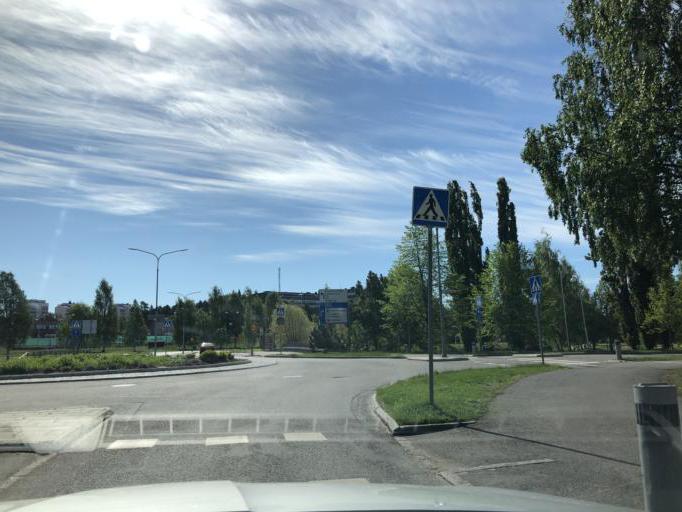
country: SE
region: Norrbotten
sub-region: Pitea Kommun
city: Pitea
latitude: 65.3157
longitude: 21.4896
